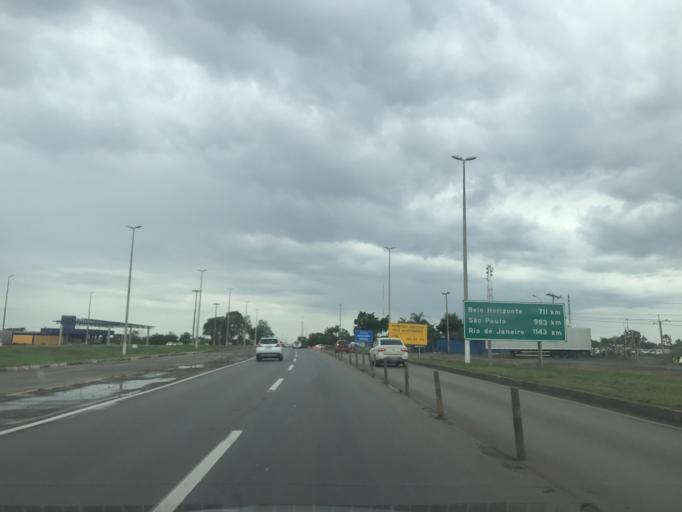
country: BR
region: Federal District
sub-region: Brasilia
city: Brasilia
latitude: -15.9812
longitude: -47.9891
